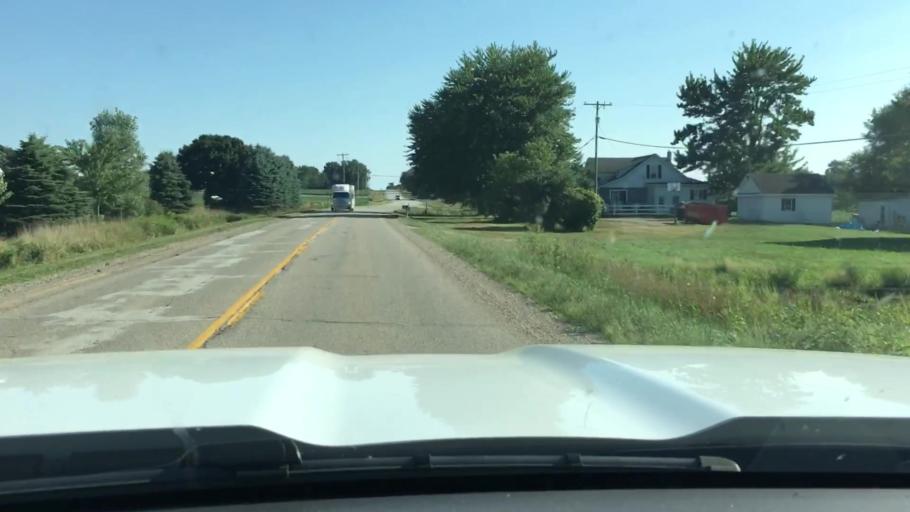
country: US
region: Michigan
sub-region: Ottawa County
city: Zeeland
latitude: 42.8580
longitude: -85.9599
